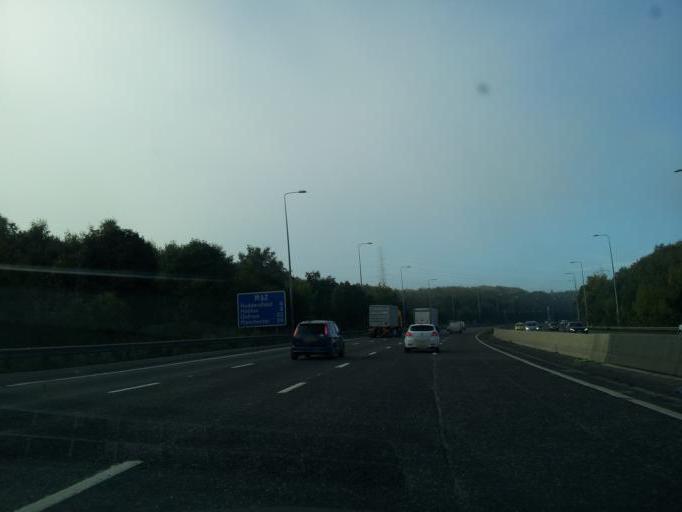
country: GB
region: England
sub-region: Calderdale
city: Brighouse
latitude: 53.6888
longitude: -1.7598
